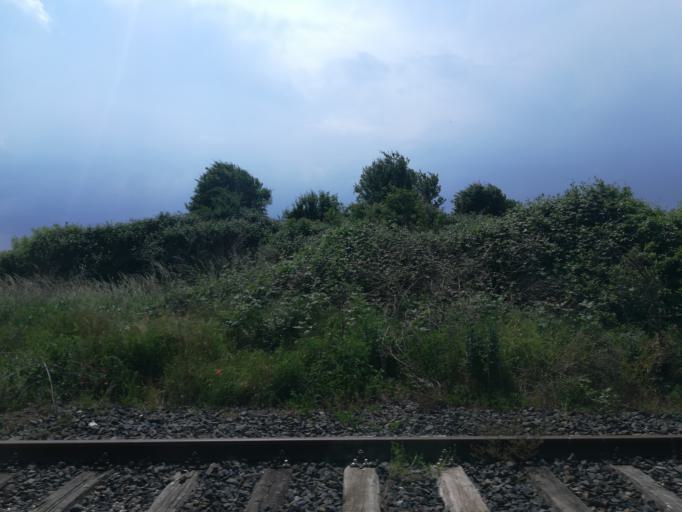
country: IT
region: Veneto
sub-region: Provincia di Vicenza
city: Dueville
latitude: 45.6380
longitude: 11.5432
